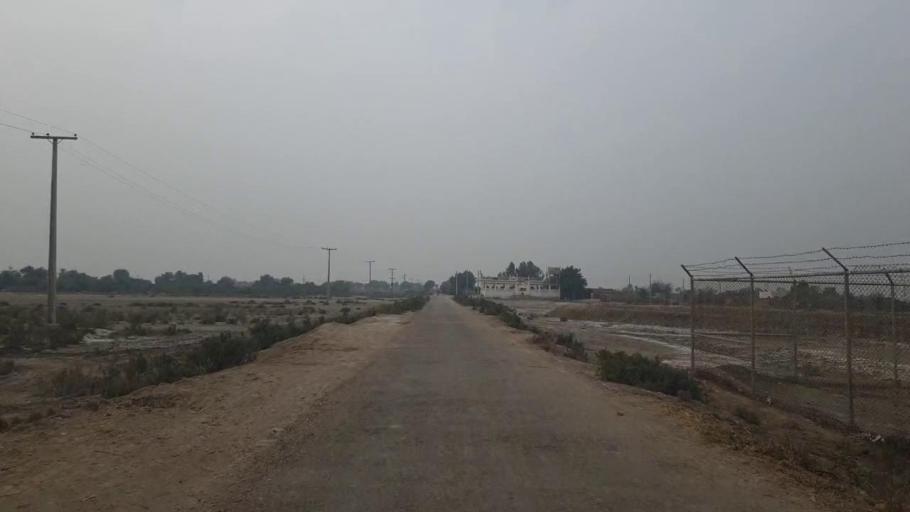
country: PK
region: Sindh
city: Shahdadpur
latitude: 25.8725
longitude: 68.6340
